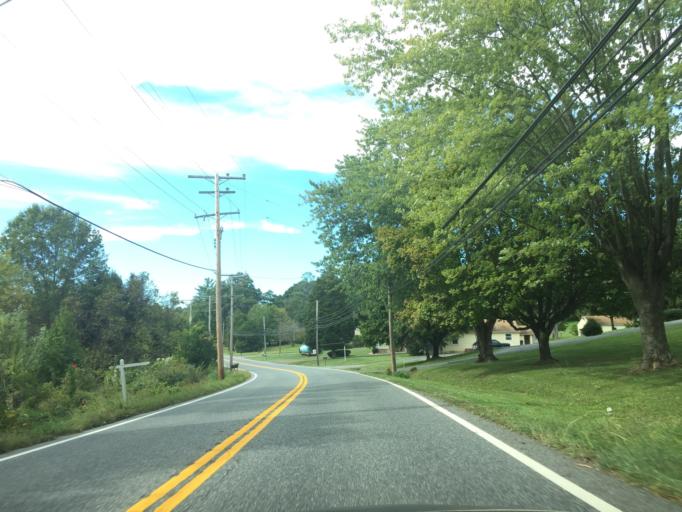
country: US
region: Maryland
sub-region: Harford County
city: Joppatowne
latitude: 39.4324
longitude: -76.3643
